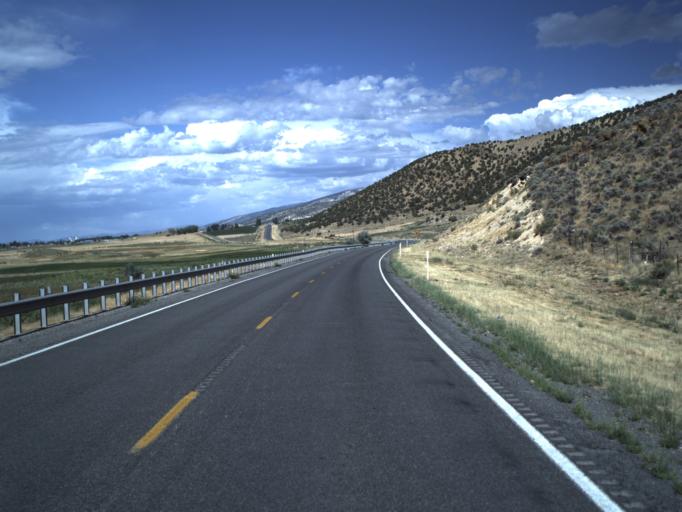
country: US
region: Utah
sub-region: Sanpete County
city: Manti
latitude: 39.2322
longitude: -111.6657
